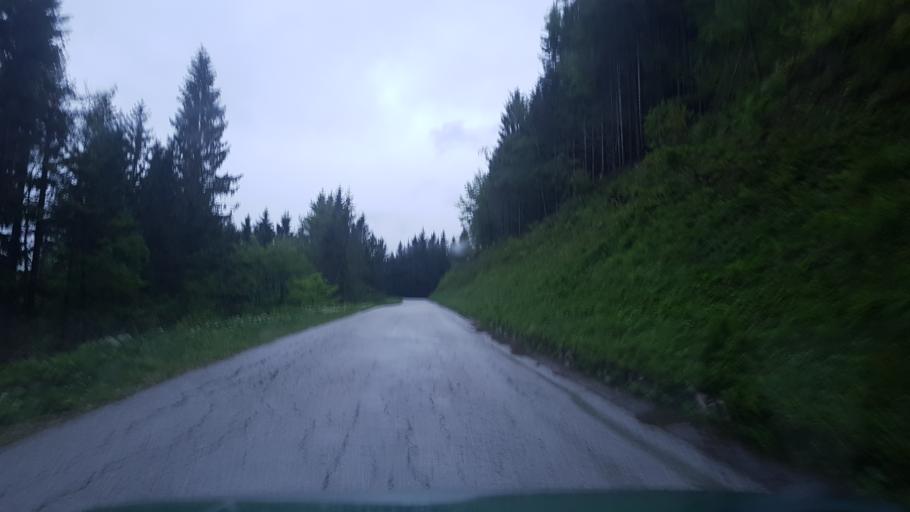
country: SI
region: Bohinj
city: Bohinjska Bistrica
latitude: 46.2195
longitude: 14.0139
